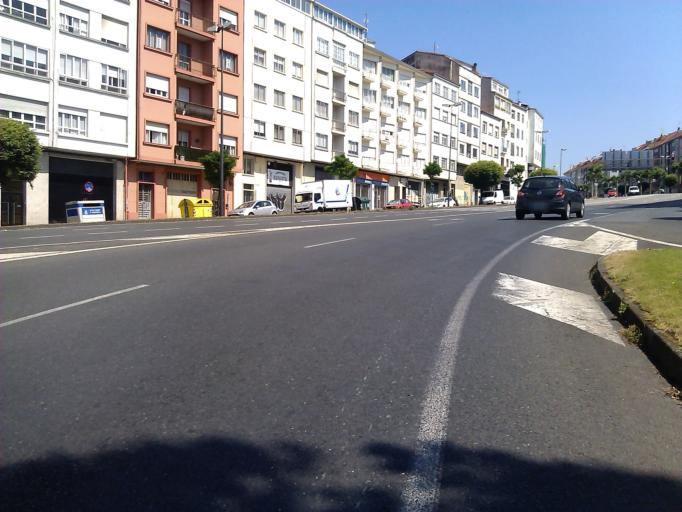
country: ES
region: Galicia
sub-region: Provincia da Coruna
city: Santiago de Compostela
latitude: 42.8785
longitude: -8.5334
